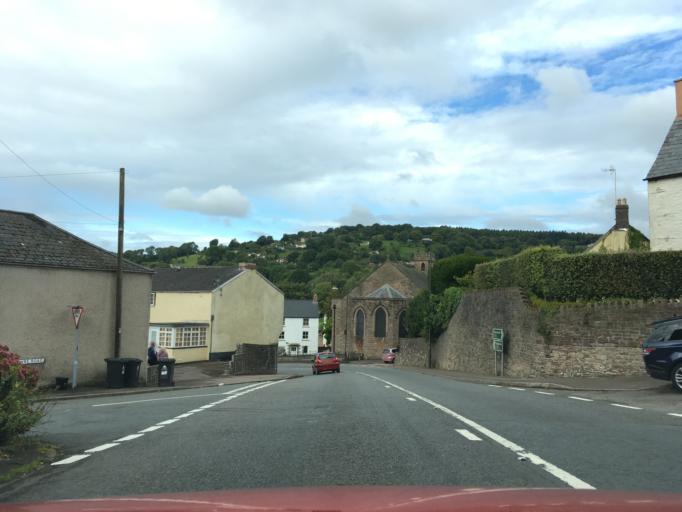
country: GB
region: England
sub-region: Gloucestershire
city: Lydney
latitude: 51.7613
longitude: -2.4754
